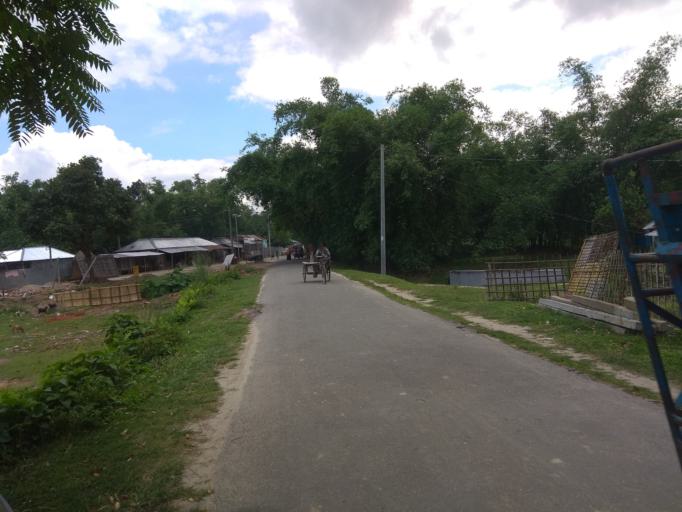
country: IN
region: West Bengal
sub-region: Koch Bihar
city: Haldibari
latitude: 26.1982
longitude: 88.9228
